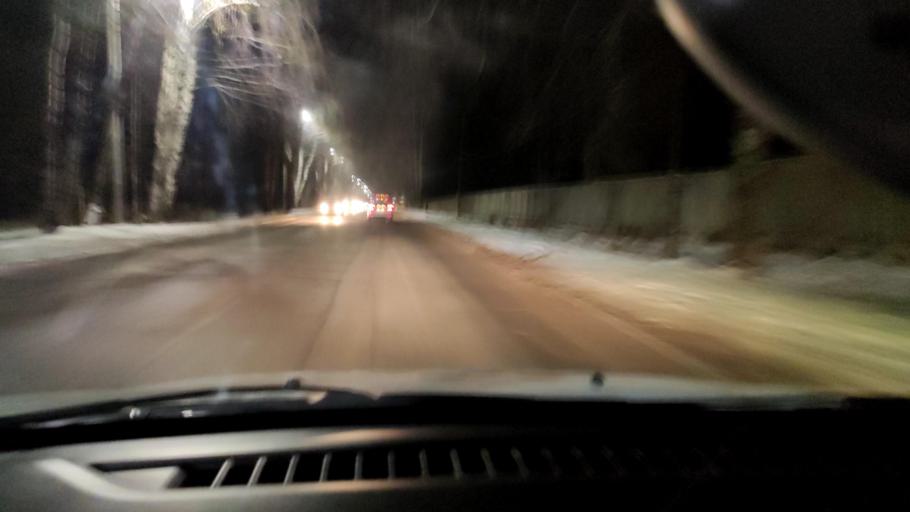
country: RU
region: Perm
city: Kultayevo
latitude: 57.9820
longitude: 55.9187
